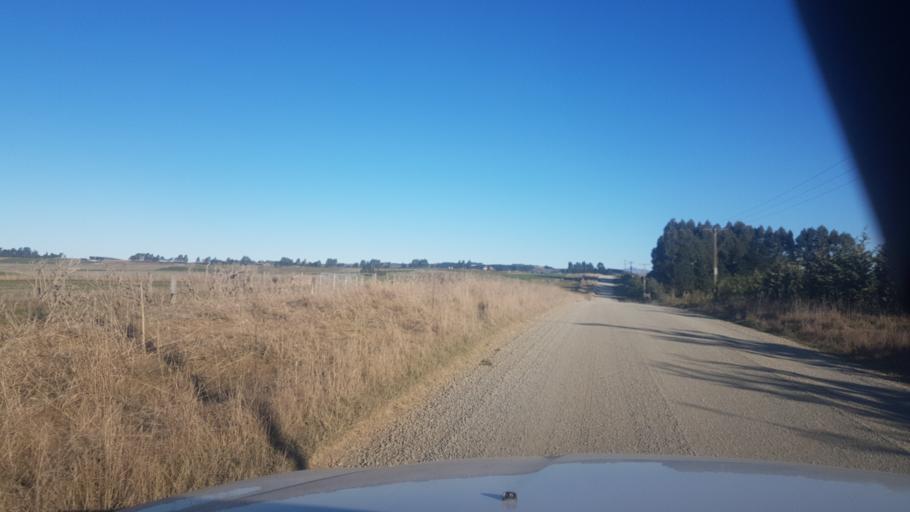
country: NZ
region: Canterbury
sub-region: Timaru District
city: Pleasant Point
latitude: -44.3481
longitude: 171.0738
